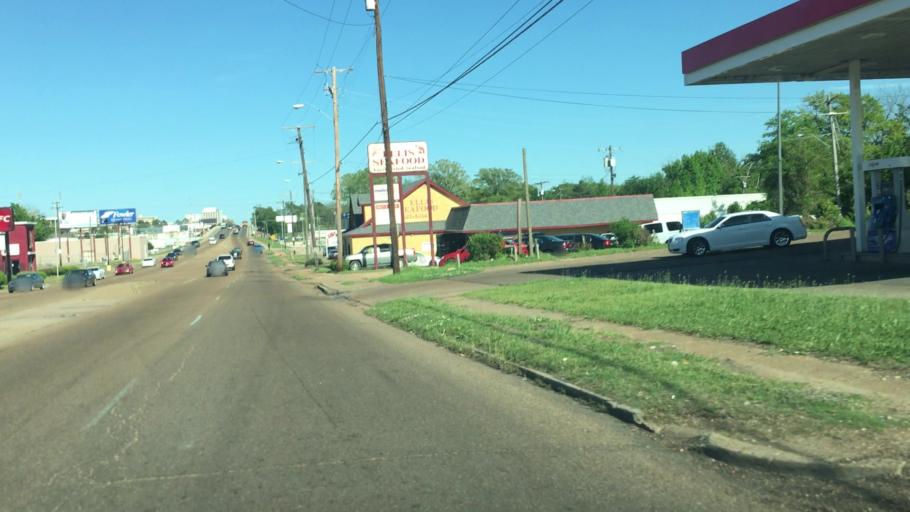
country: US
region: Mississippi
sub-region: Hinds County
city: Jackson
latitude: 32.3267
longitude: -90.1926
